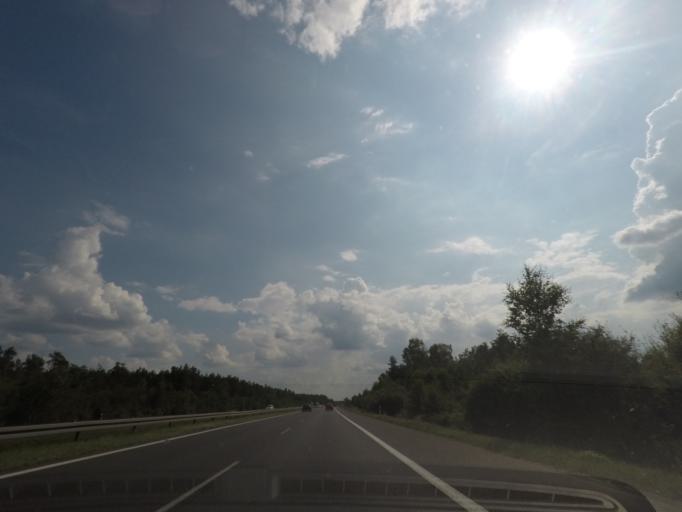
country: PL
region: Lodz Voivodeship
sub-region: Powiat radomszczanski
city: Kamiensk
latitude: 51.2486
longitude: 19.5252
